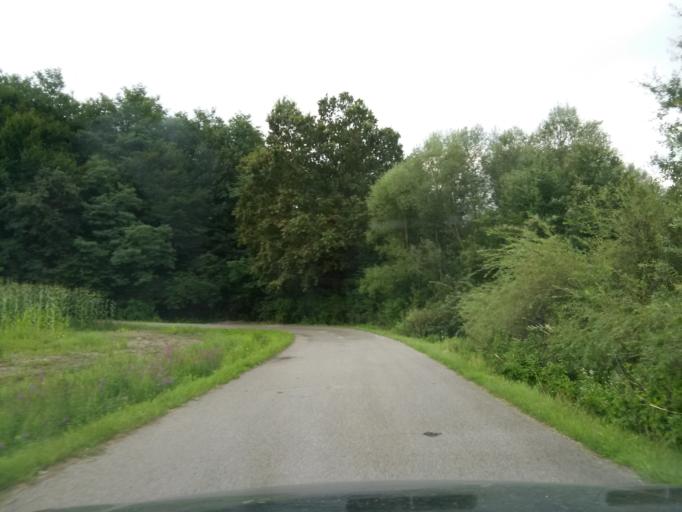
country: HR
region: Sisacko-Moslavacka
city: Glina
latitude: 45.2886
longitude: 15.9911
